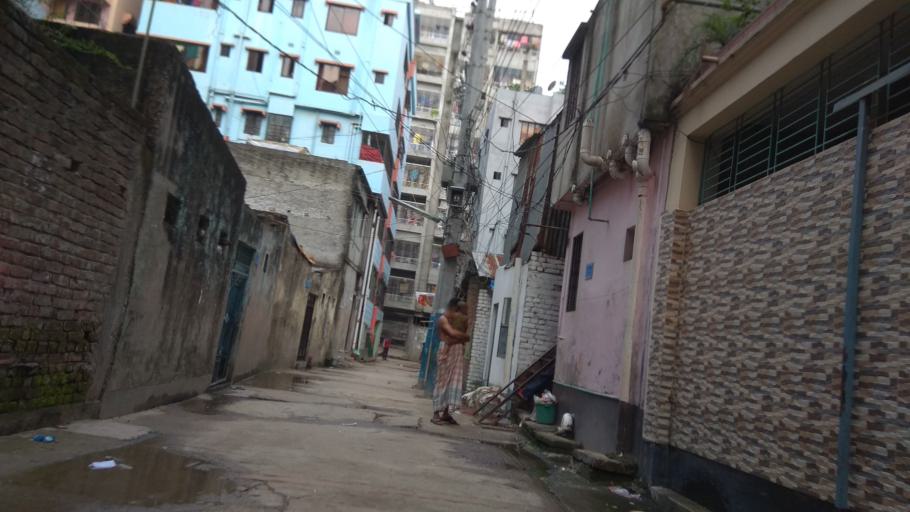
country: BD
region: Dhaka
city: Azimpur
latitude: 23.7993
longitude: 90.3594
